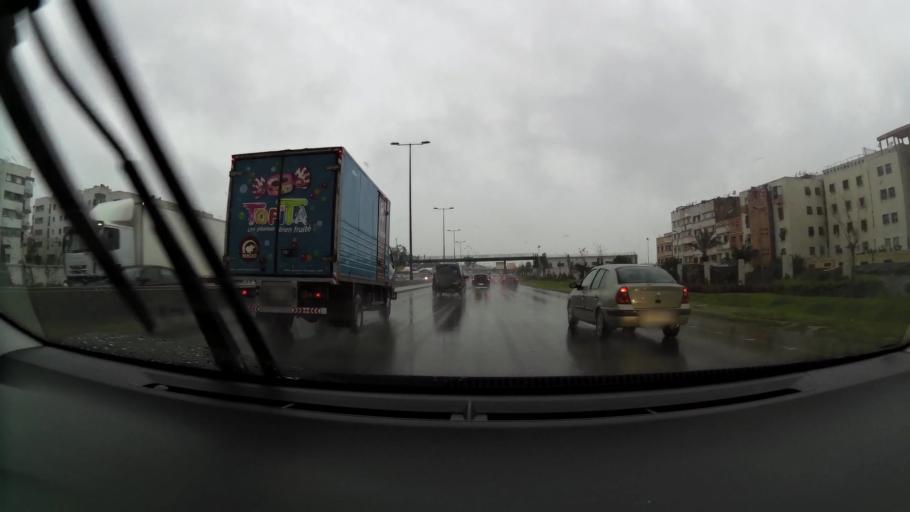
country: MA
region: Grand Casablanca
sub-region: Casablanca
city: Casablanca
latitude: 33.5627
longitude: -7.5840
